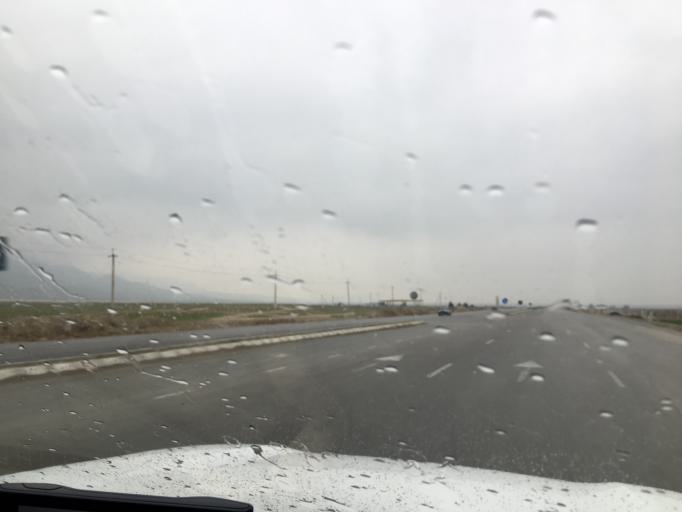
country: TM
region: Ahal
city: Annau
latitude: 37.7918
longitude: 58.8226
